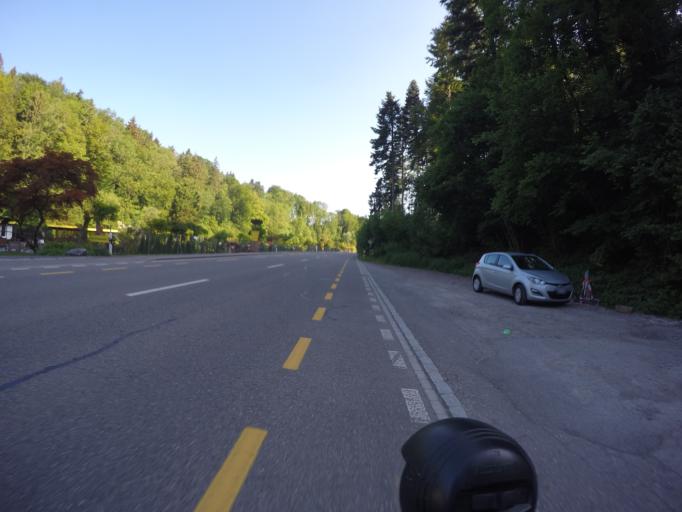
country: CH
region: Zurich
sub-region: Bezirk Winterthur
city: Toss
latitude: 47.4704
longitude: 8.7044
